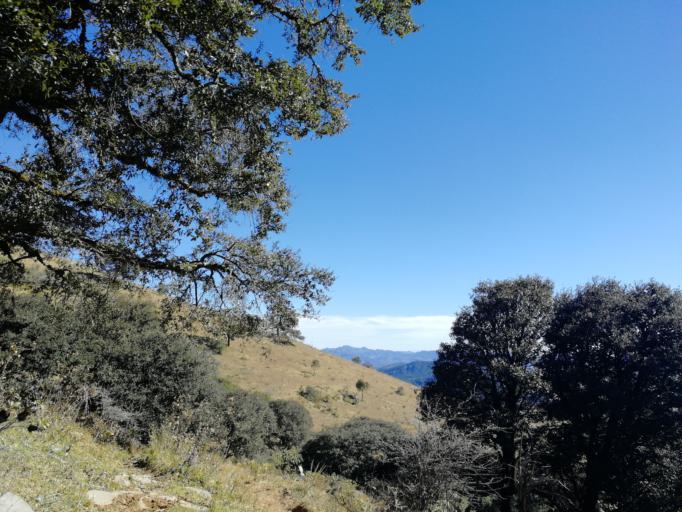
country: MX
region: San Luis Potosi
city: Zaragoza
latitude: 22.0070
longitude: -100.6150
